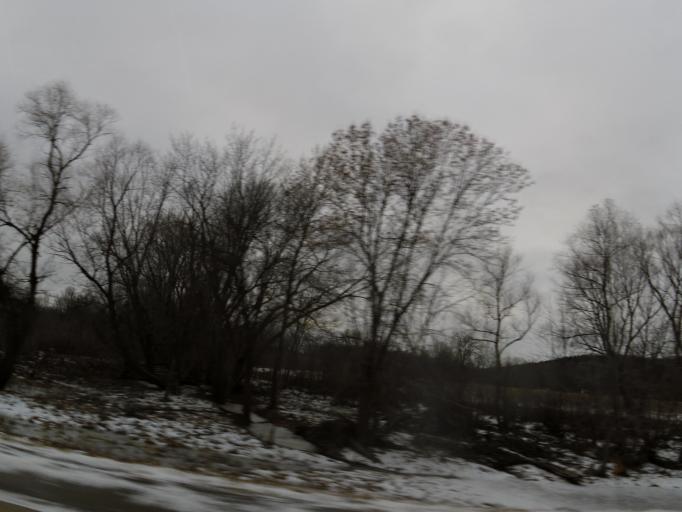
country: US
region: Minnesota
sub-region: Scott County
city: Jordan
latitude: 44.7021
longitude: -93.6449
